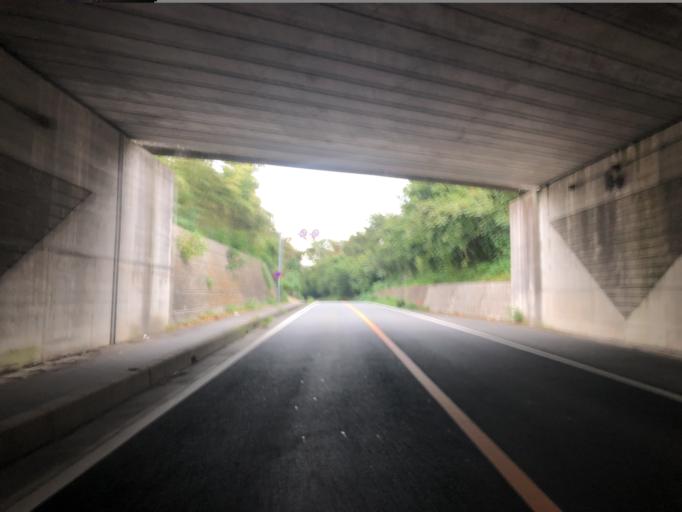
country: JP
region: Saitama
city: Fukiage-fujimi
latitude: 36.0536
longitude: 139.4074
